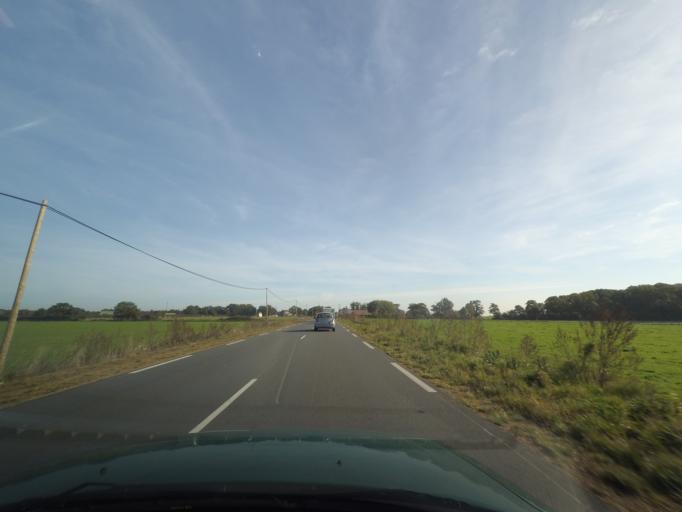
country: FR
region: Pays de la Loire
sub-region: Departement de Maine-et-Loire
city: Torfou
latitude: 47.0289
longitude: -1.0968
